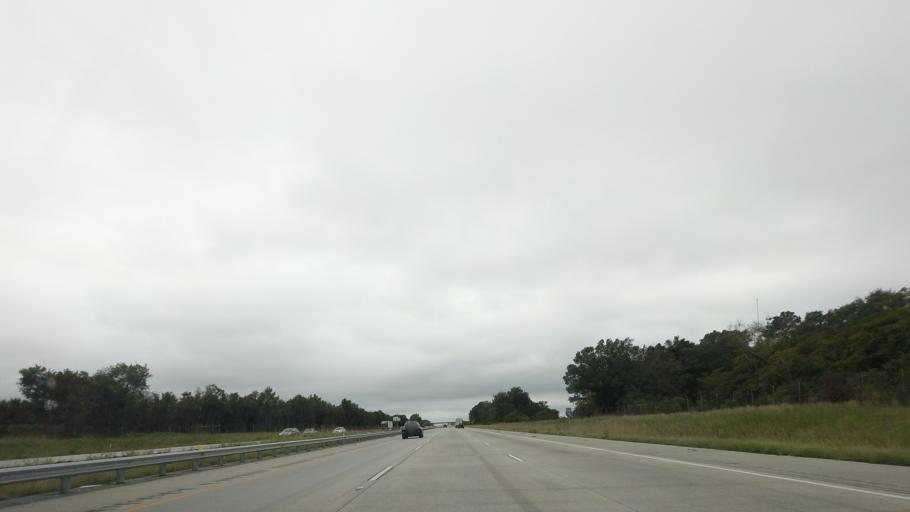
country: US
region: Georgia
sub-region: Dooly County
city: Unadilla
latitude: 32.1846
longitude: -83.7495
